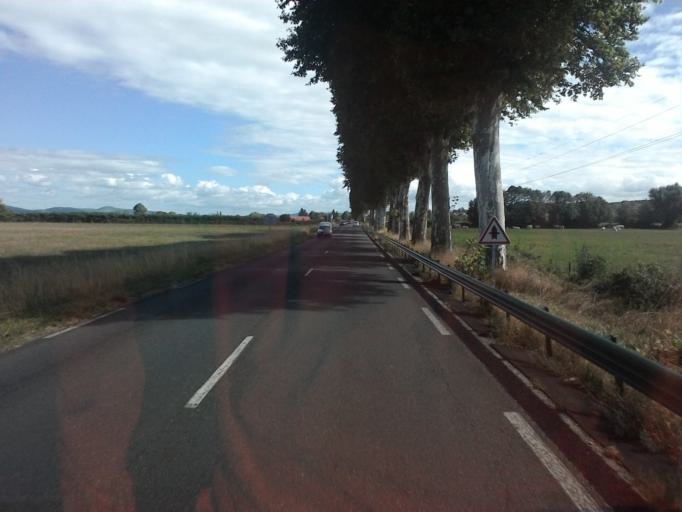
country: FR
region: Rhone-Alpes
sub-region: Departement de l'Ain
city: Ambronay
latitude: 45.9905
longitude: 5.3519
